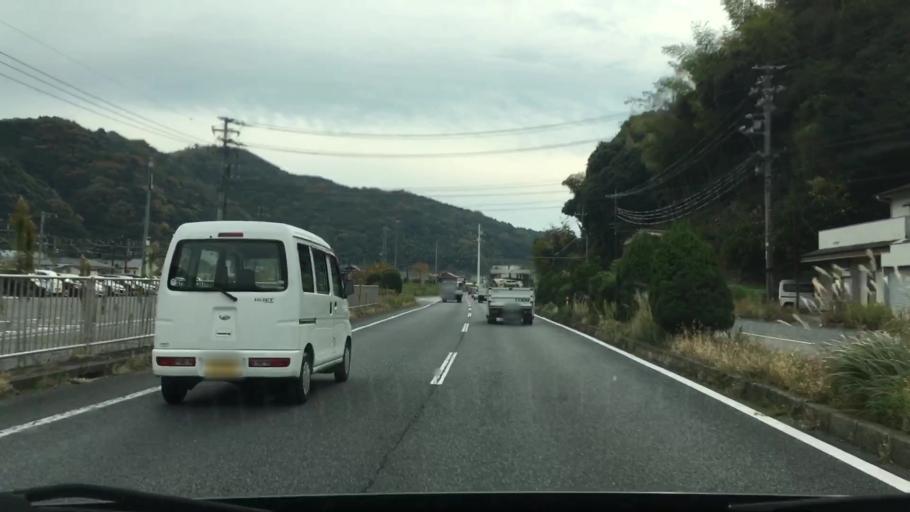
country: JP
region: Yamaguchi
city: Tokuyama
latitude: 34.0726
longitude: 131.7039
